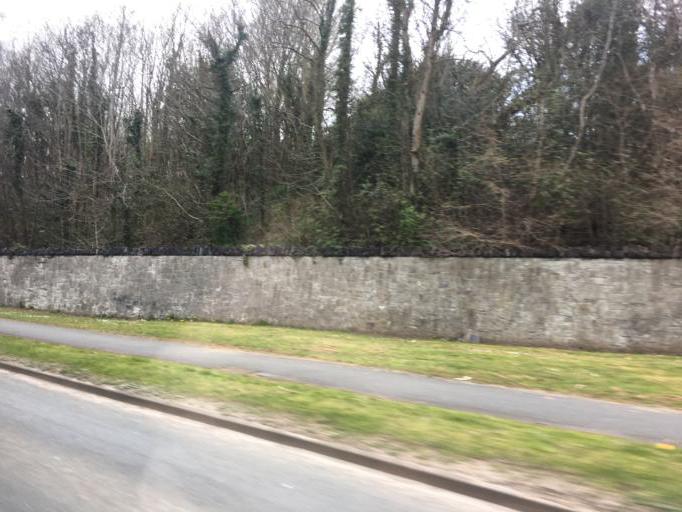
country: GB
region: Wales
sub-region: Gwynedd
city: Y Felinheli
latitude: 53.1946
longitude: -4.1863
